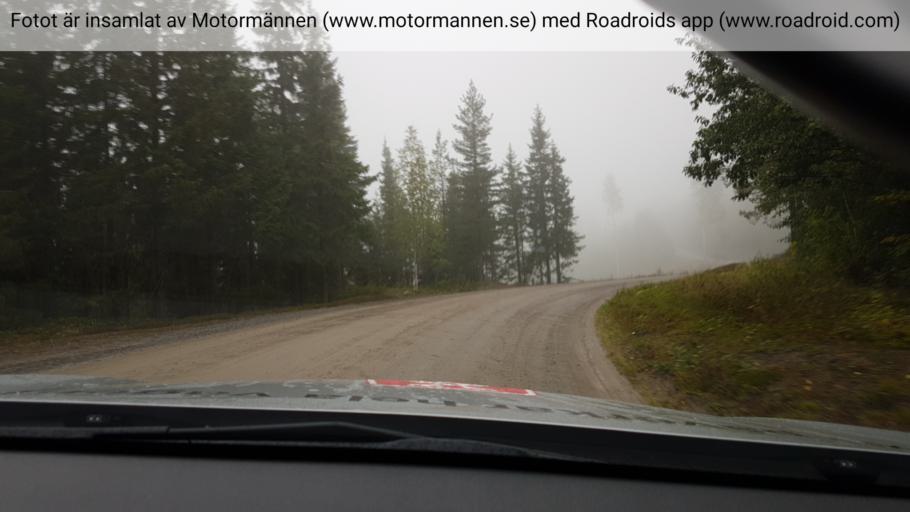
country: SE
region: Vaesterbotten
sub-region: Vannas Kommun
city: Vannasby
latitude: 64.0829
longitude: 20.0456
